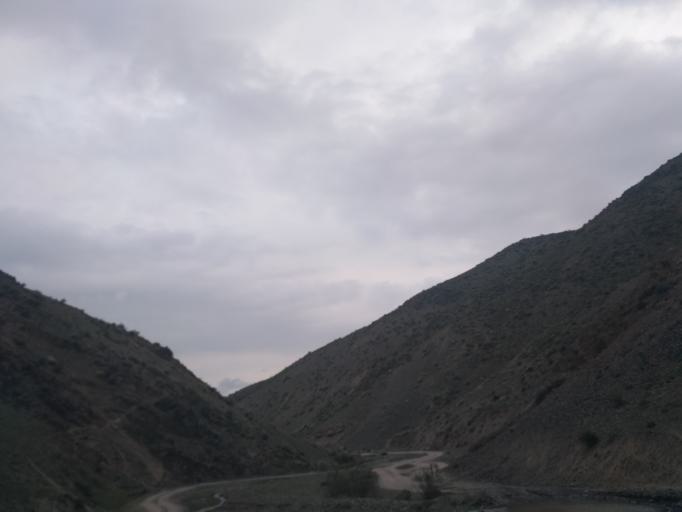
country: UZ
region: Jizzax
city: Zomin
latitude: 39.8589
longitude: 68.3855
